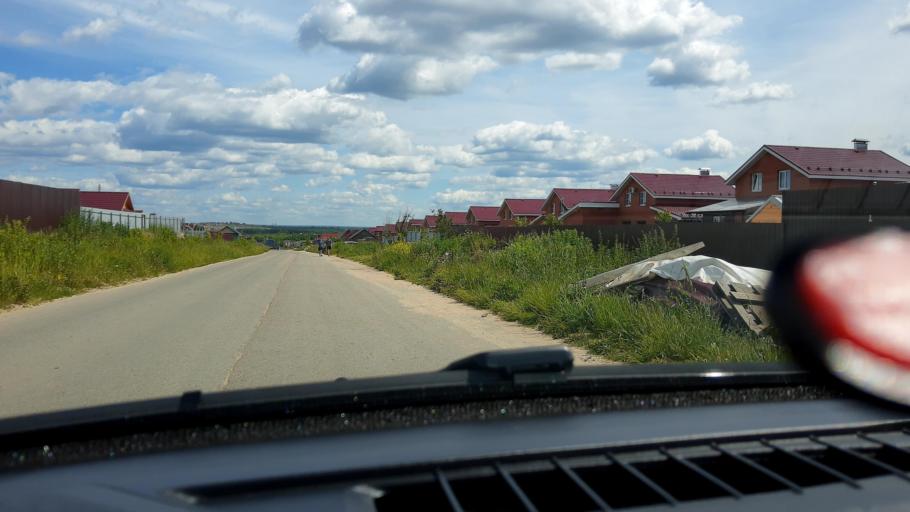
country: RU
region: Nizjnij Novgorod
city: Afonino
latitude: 56.1969
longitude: 44.0812
